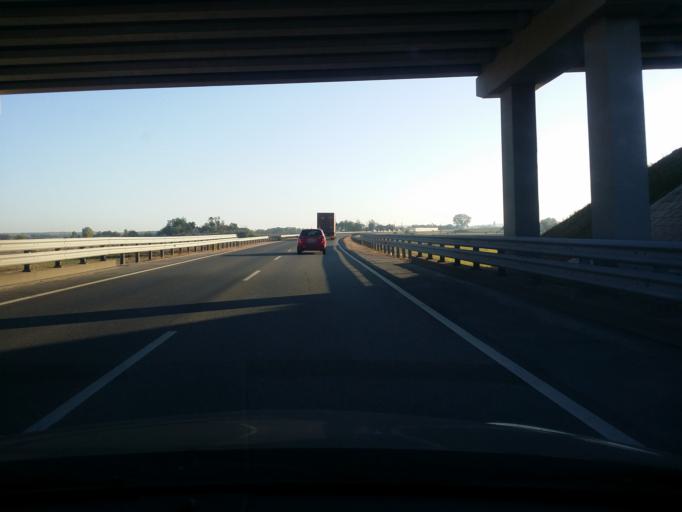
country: HU
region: Bacs-Kiskun
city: Kecskemet
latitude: 46.9485
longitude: 19.6706
